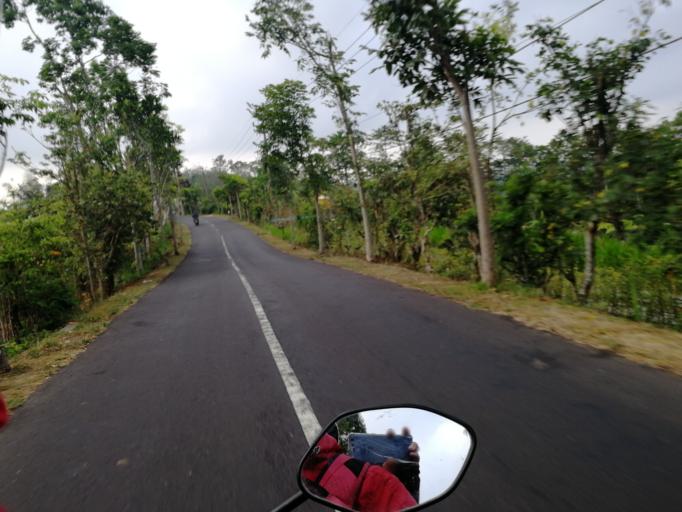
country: ID
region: Bali
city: Peneng
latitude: -8.2524
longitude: 115.2448
